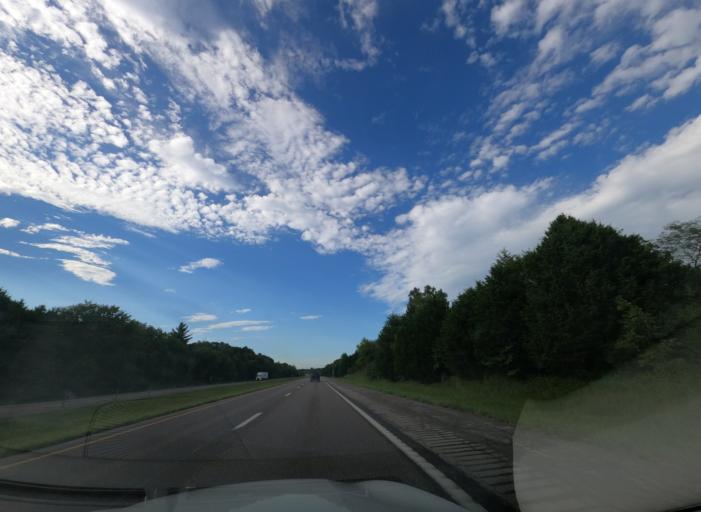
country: US
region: Missouri
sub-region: Jefferson County
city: Crystal City
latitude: 38.1175
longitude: -90.3088
